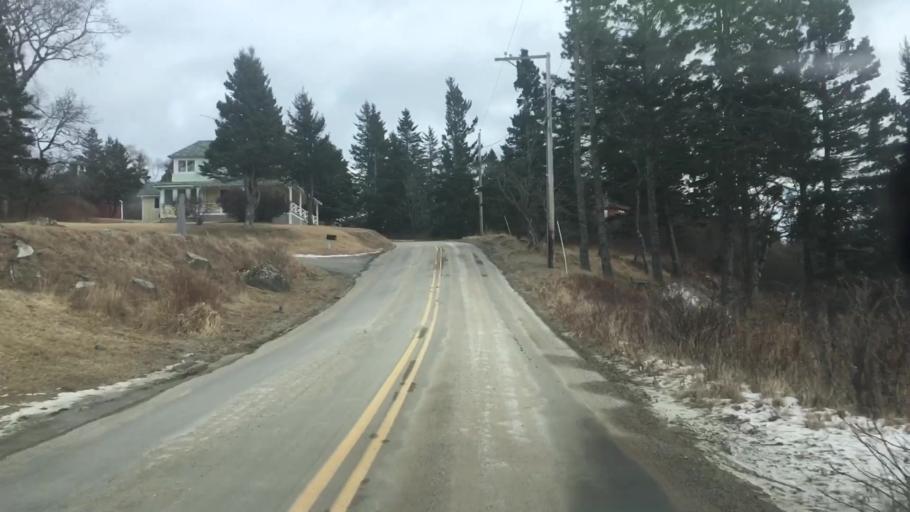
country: US
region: Maine
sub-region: Washington County
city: Machias
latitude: 44.6115
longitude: -67.4819
